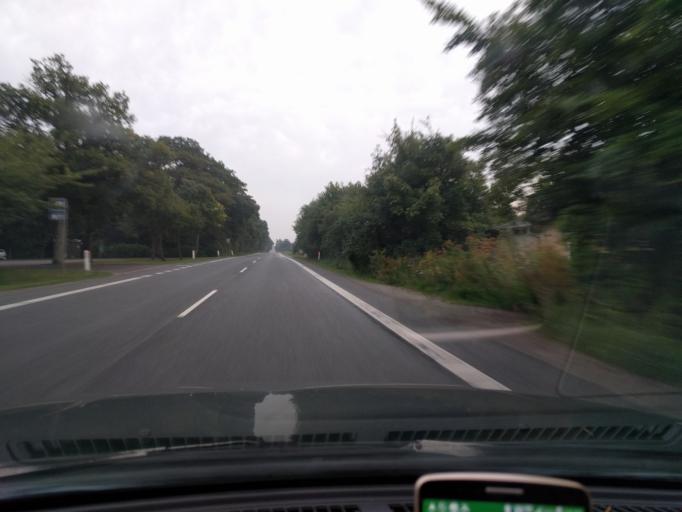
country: DK
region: Zealand
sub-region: Guldborgsund Kommune
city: Norre Alslev
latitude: 54.9277
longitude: 11.8726
